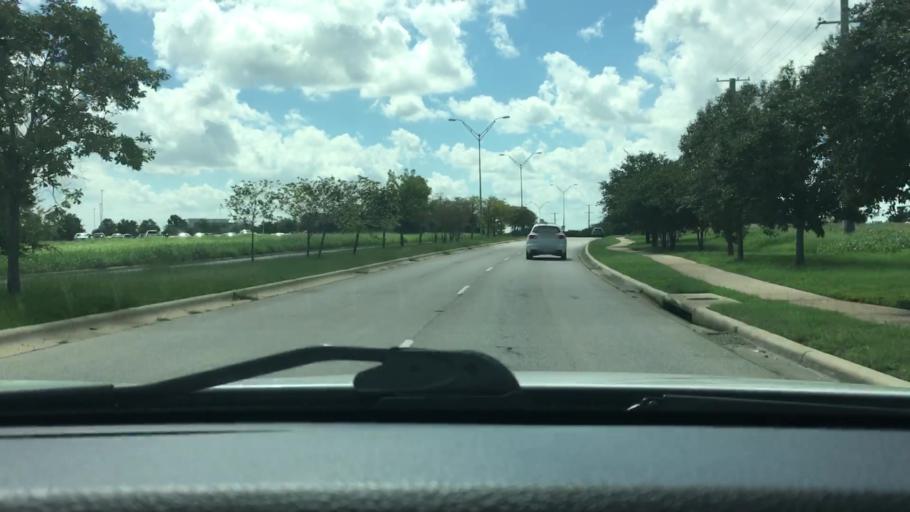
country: US
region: Texas
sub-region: Williamson County
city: Round Rock
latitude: 30.5662
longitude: -97.6868
